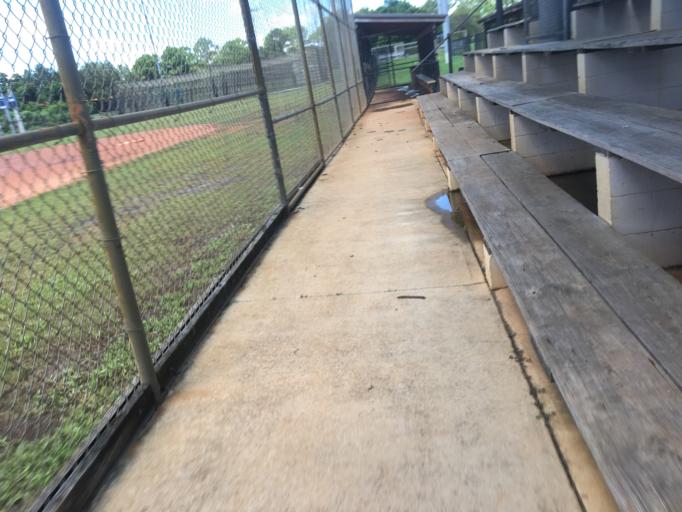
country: US
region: Florida
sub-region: Martin County
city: Palm City
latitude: 27.1782
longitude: -80.2723
